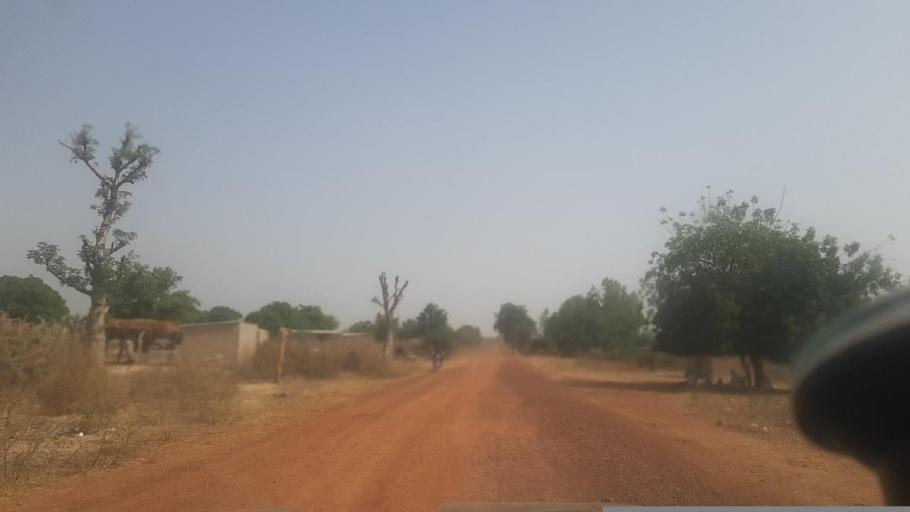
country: ML
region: Segou
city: Segou
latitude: 12.9322
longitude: -6.2873
